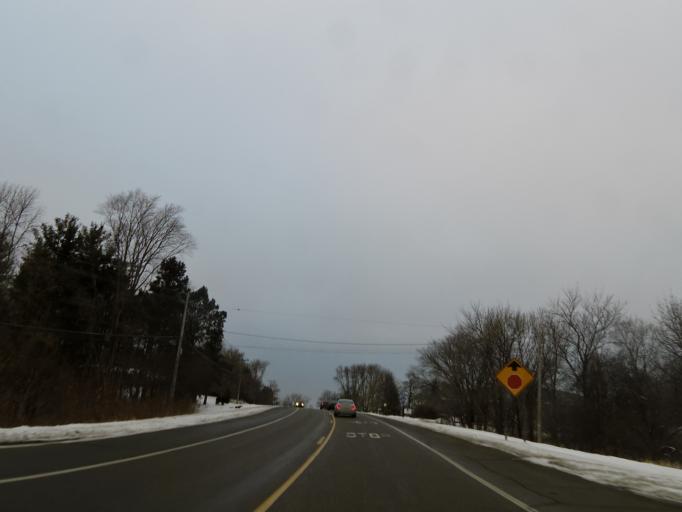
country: US
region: Minnesota
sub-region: Washington County
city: Newport
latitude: 44.8900
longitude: -92.9879
